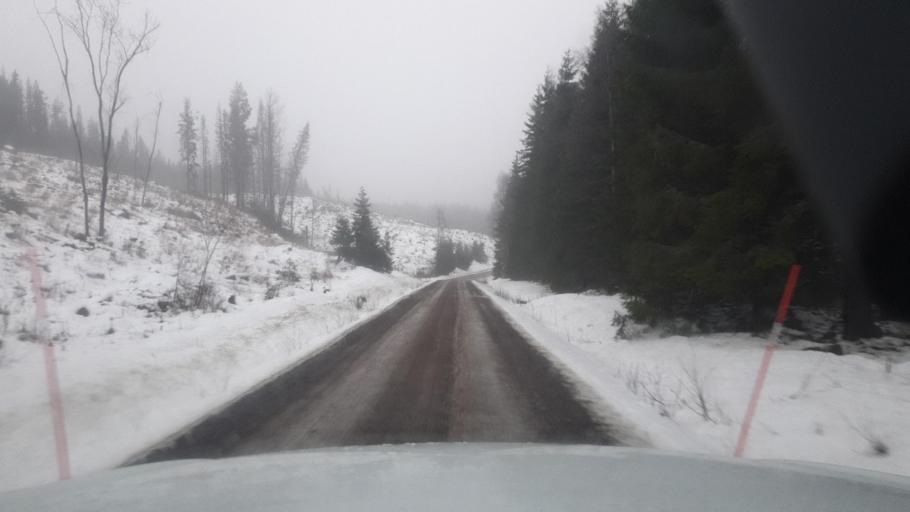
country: SE
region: Vaermland
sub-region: Eda Kommun
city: Charlottenberg
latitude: 60.0453
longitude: 12.6304
